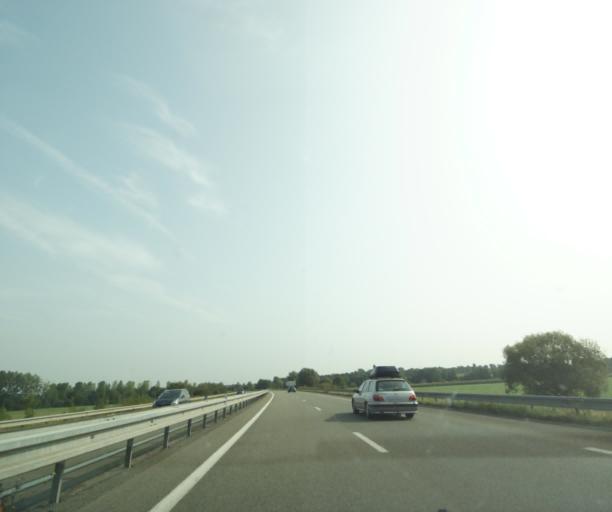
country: FR
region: Pays de la Loire
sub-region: Departement de la Sarthe
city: Montbizot
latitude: 48.1814
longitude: 0.1647
